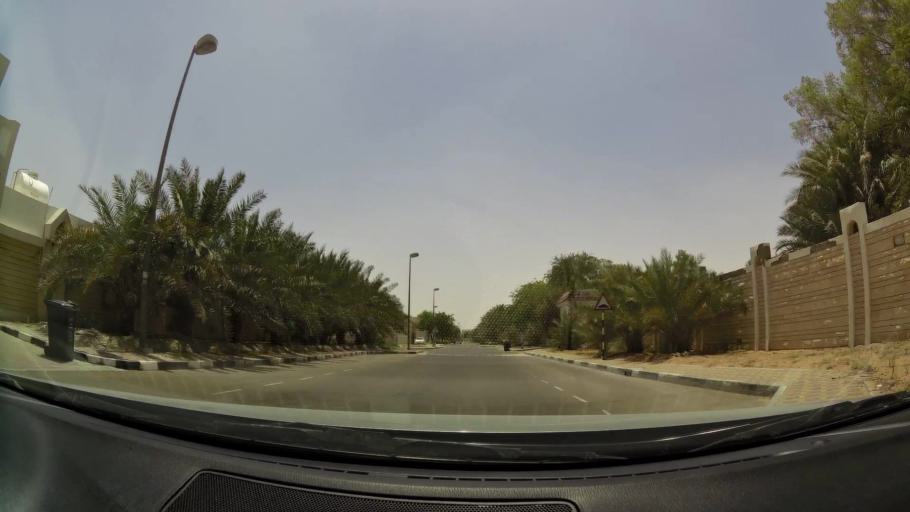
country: AE
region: Abu Dhabi
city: Al Ain
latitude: 24.2529
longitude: 55.7126
